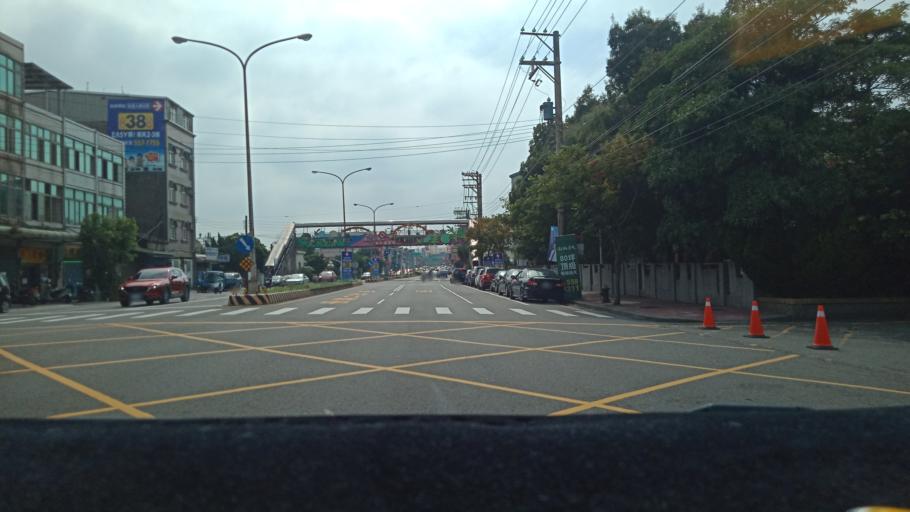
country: TW
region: Taiwan
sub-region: Hsinchu
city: Zhubei
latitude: 24.8721
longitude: 120.9989
